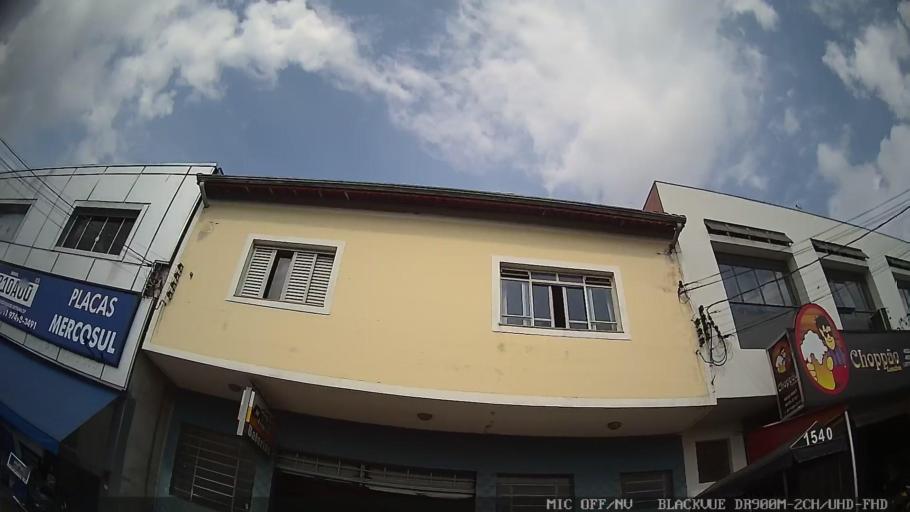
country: BR
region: Sao Paulo
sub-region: Braganca Paulista
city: Braganca Paulista
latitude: -22.9537
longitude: -46.5450
